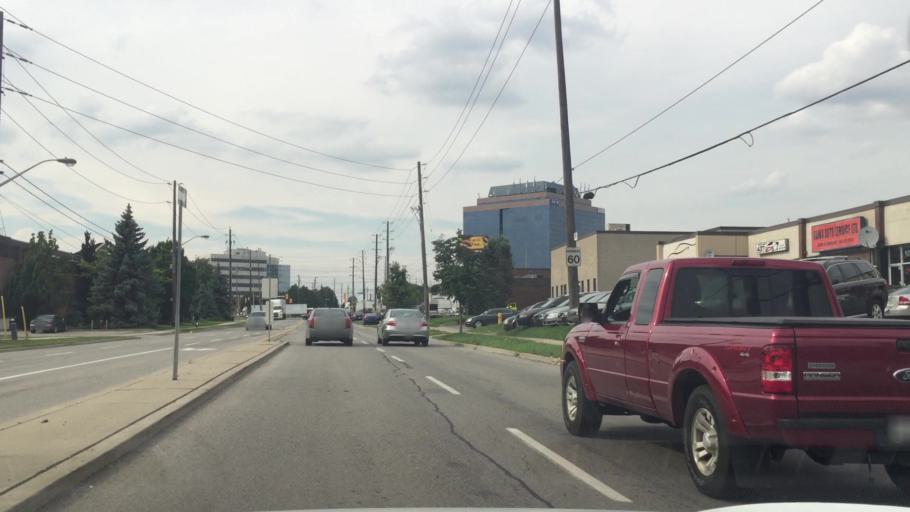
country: CA
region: Ontario
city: Concord
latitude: 43.7686
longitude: -79.5423
